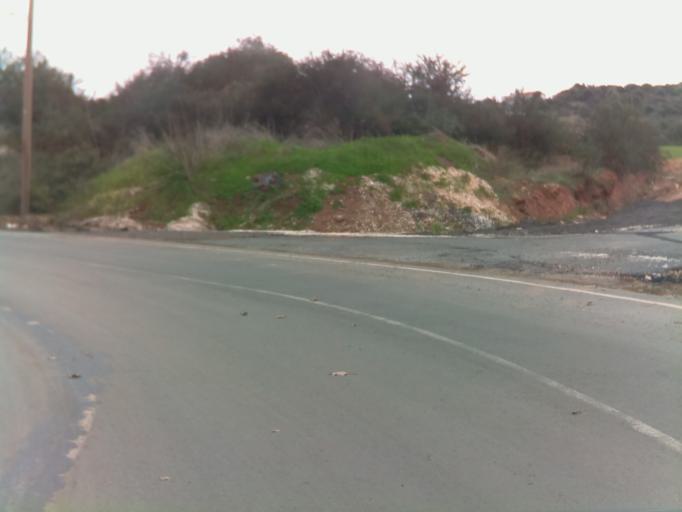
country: CY
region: Pafos
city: Polis
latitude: 35.0435
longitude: 32.3626
